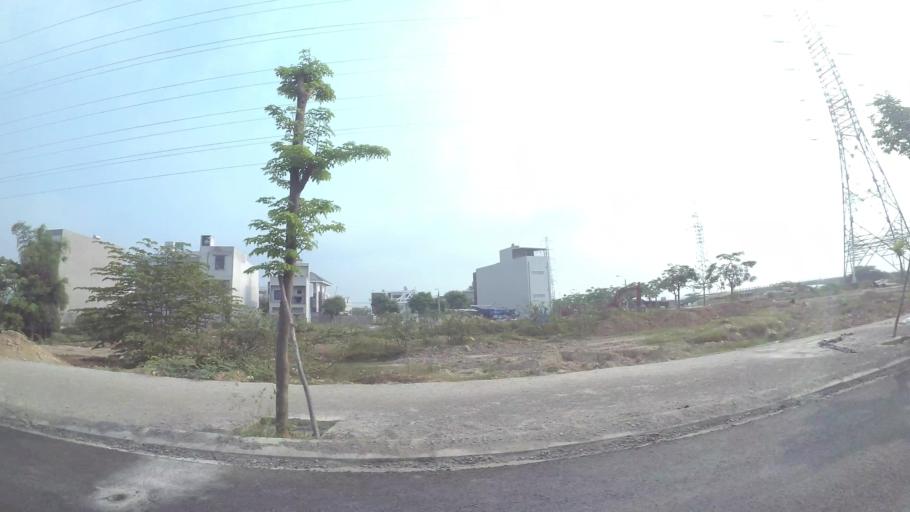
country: VN
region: Da Nang
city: Ngu Hanh Son
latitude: 16.0149
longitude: 108.2324
